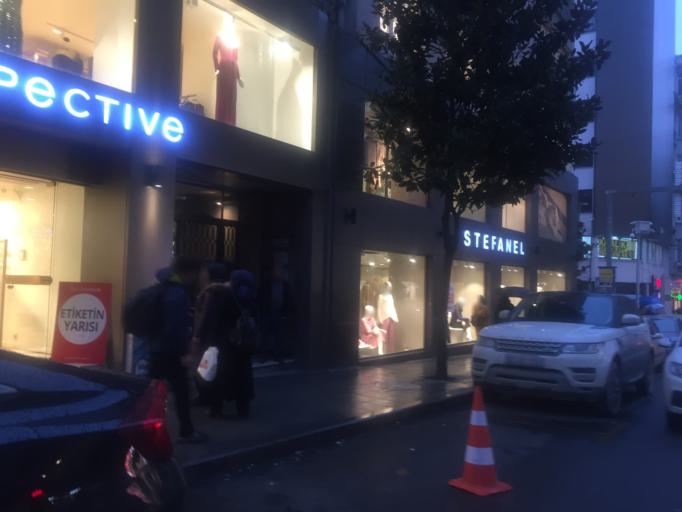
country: TR
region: Istanbul
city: Sisli
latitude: 41.0520
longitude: 28.9912
